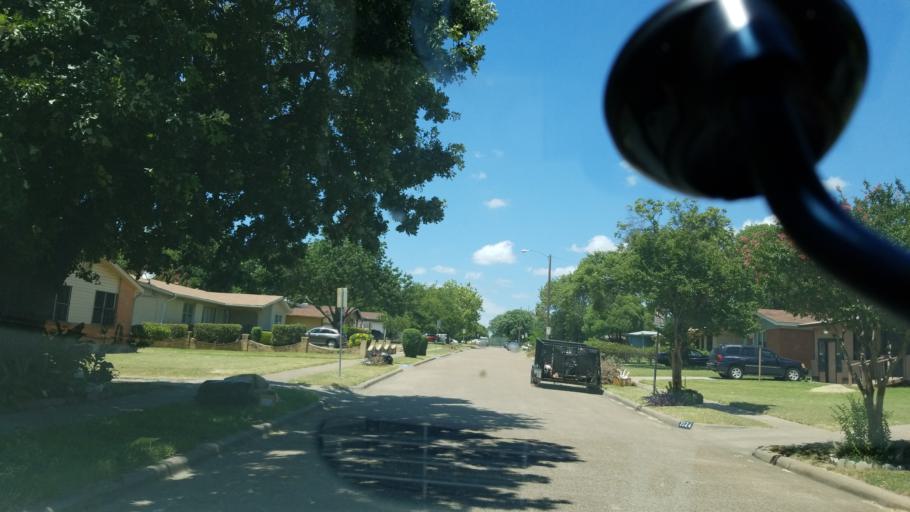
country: US
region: Texas
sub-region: Dallas County
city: Cockrell Hill
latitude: 32.6963
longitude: -96.8169
